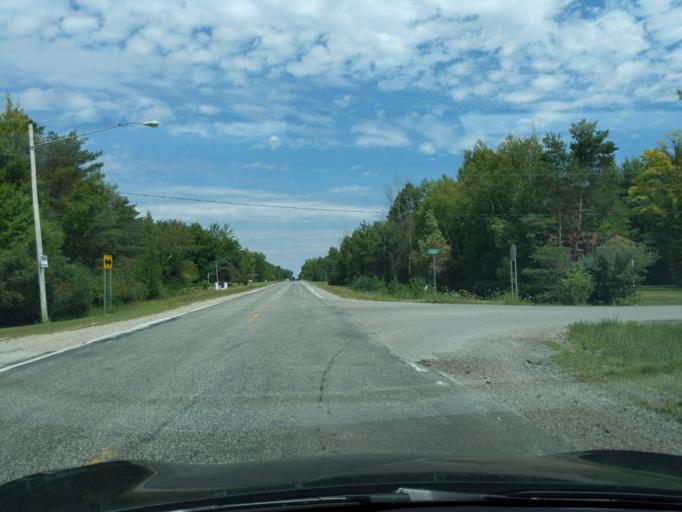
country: US
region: Michigan
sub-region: Gratiot County
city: Breckenridge
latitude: 43.4481
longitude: -84.3700
